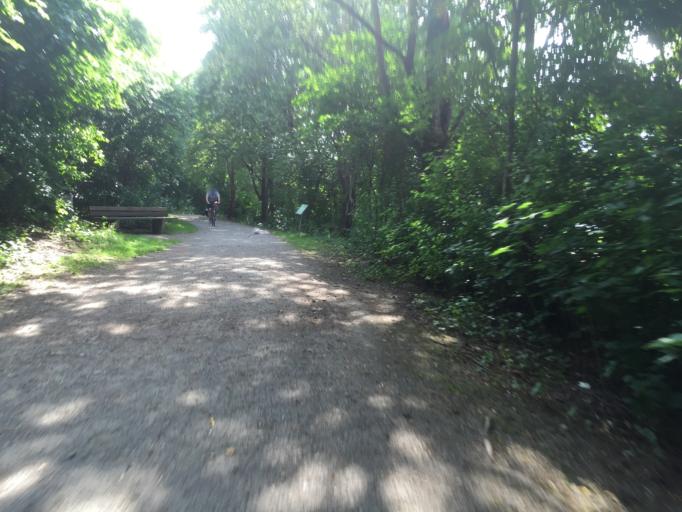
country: DE
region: Bavaria
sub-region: Upper Bavaria
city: Neubiberg
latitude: 48.1055
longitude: 11.6316
